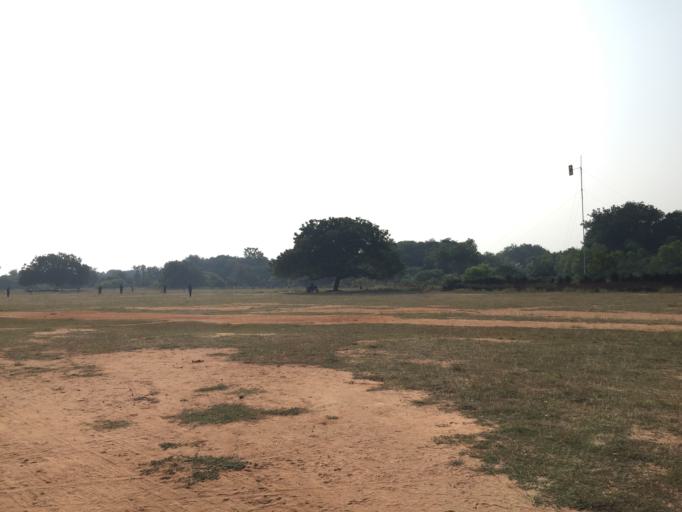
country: IN
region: Tamil Nadu
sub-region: Villupuram
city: Auroville
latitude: 12.0003
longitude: 79.8060
